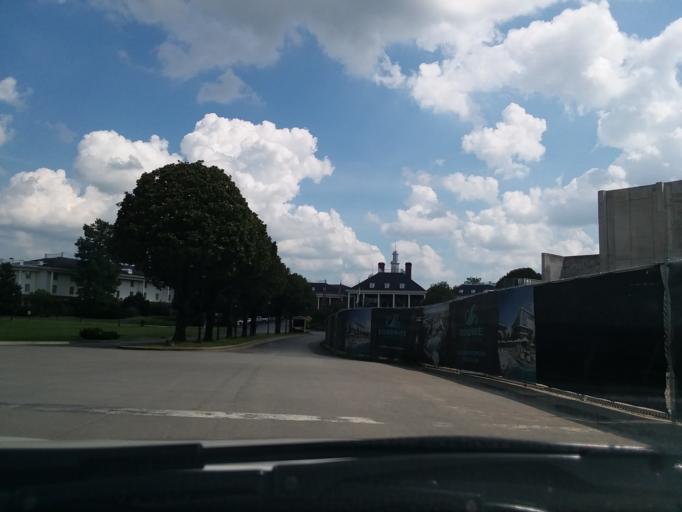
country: US
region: Tennessee
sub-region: Davidson County
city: Lakewood
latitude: 36.2144
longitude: -86.6939
